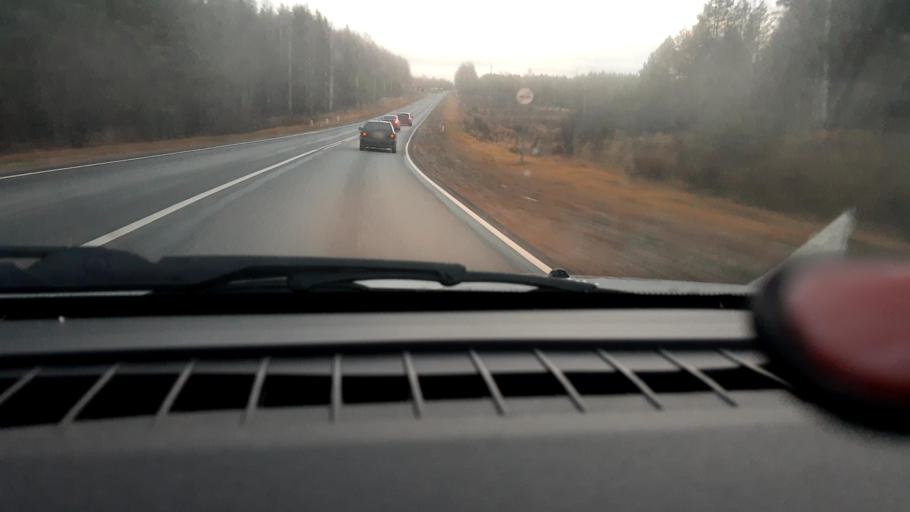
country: RU
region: Nizjnij Novgorod
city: Krasnyye Baki
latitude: 57.0220
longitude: 45.1174
